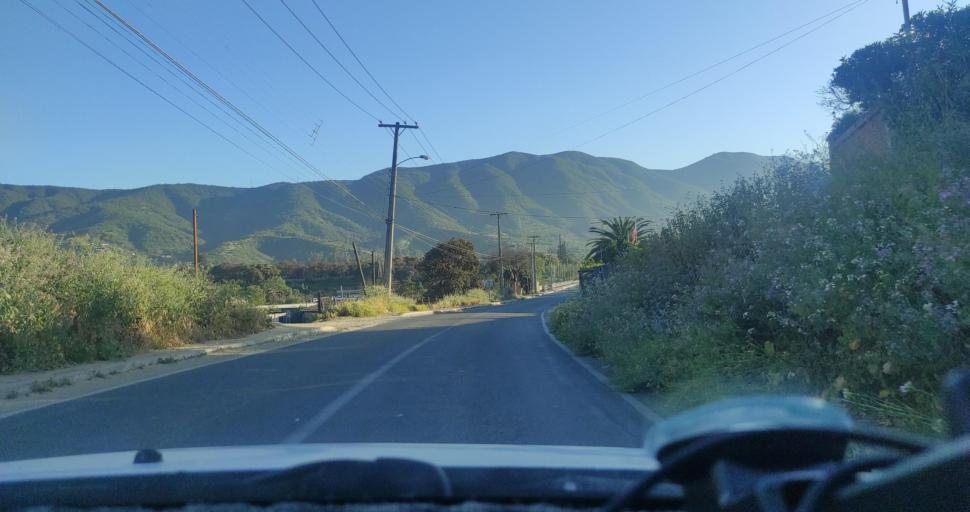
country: CL
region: Valparaiso
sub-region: Provincia de Marga Marga
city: Limache
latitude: -33.0014
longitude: -71.2239
